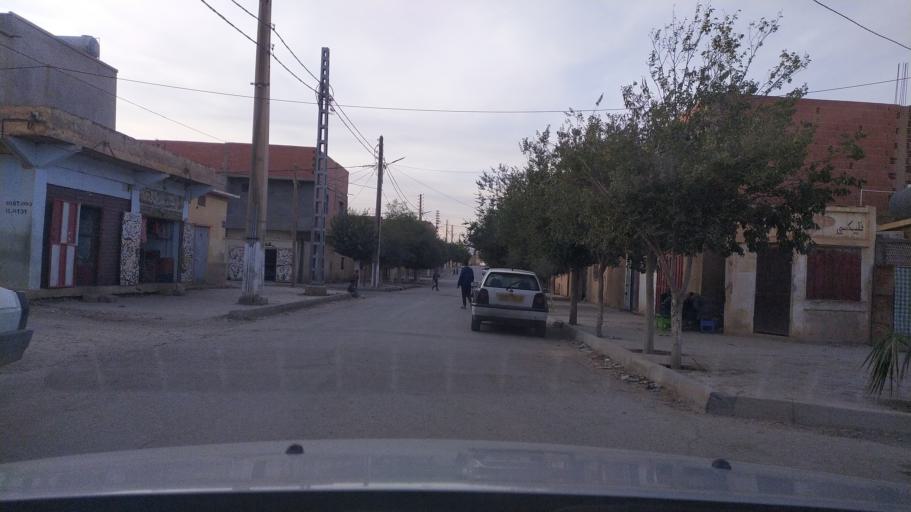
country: DZ
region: Tiaret
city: Frenda
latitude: 34.8997
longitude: 1.2378
